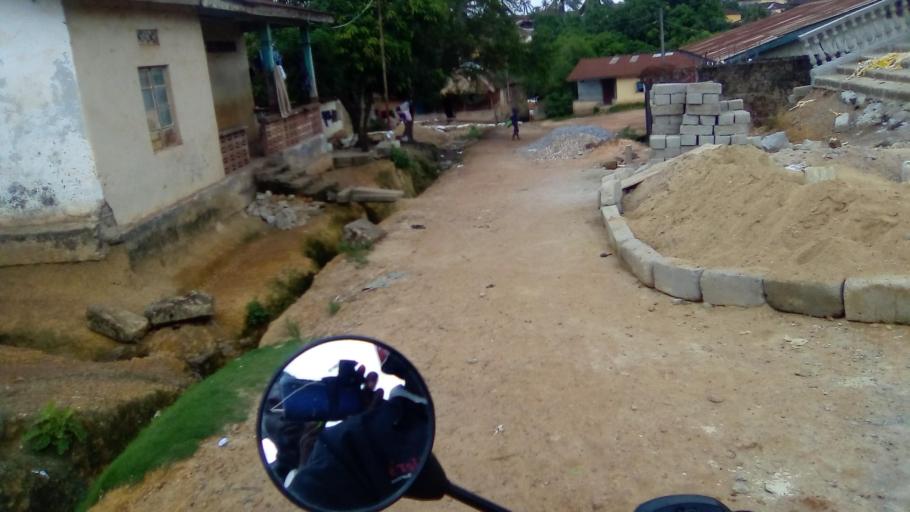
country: SL
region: Southern Province
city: Bo
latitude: 7.9610
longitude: -11.7320
